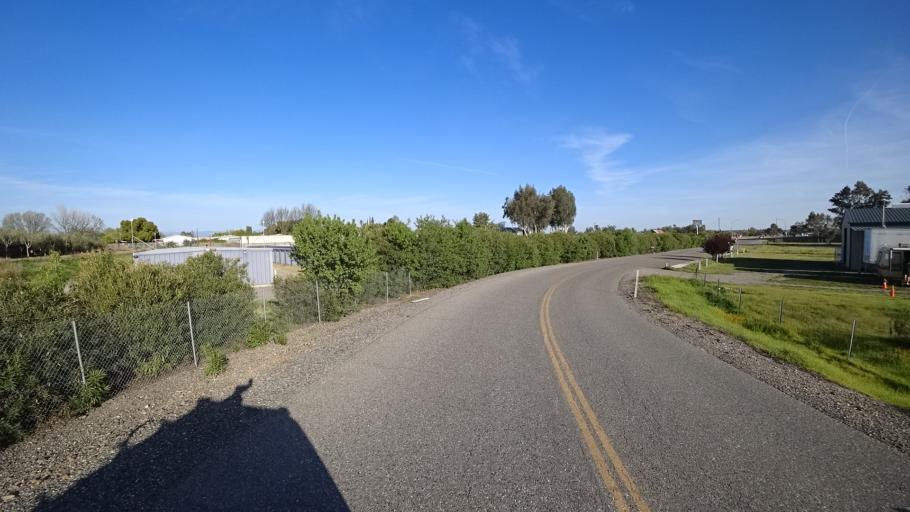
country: US
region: California
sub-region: Glenn County
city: Orland
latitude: 39.7386
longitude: -122.2072
